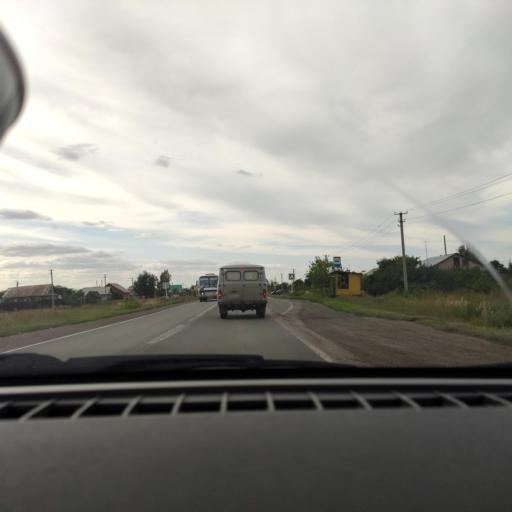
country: RU
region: Samara
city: Krasnyy Yar
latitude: 53.4433
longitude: 50.5303
